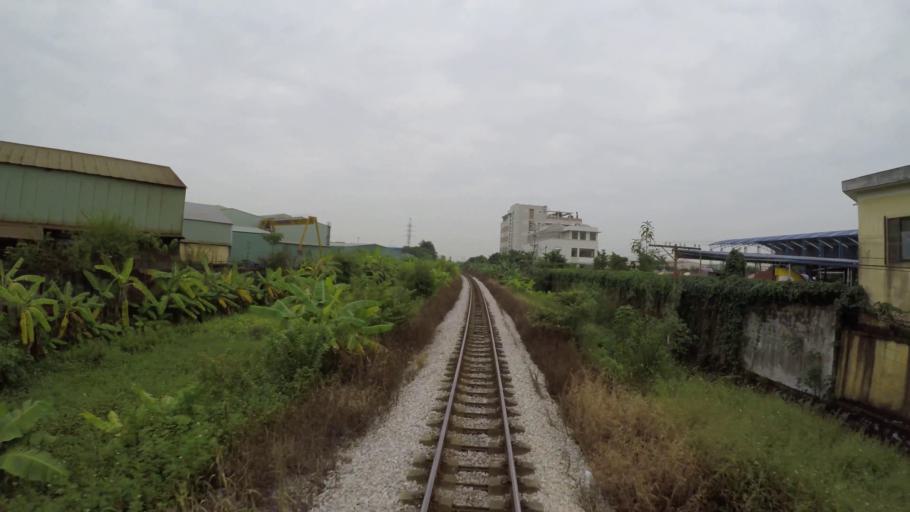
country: VN
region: Hai Phong
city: An Duong
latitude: 20.8991
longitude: 106.5803
